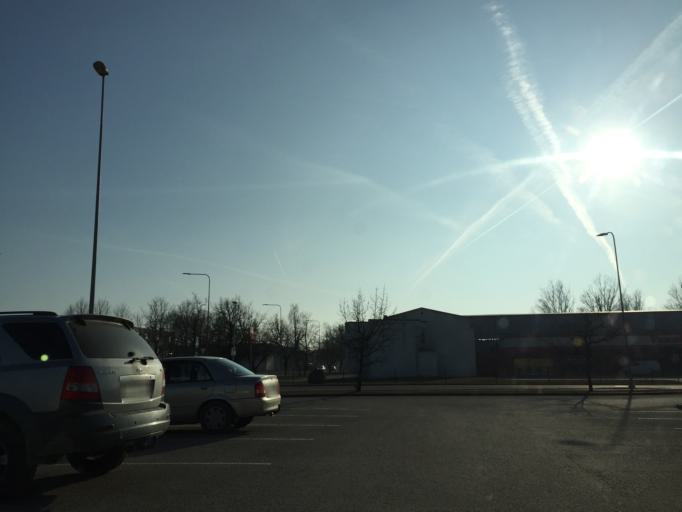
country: EE
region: Saare
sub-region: Kuressaare linn
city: Kuressaare
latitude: 58.2630
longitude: 22.5075
